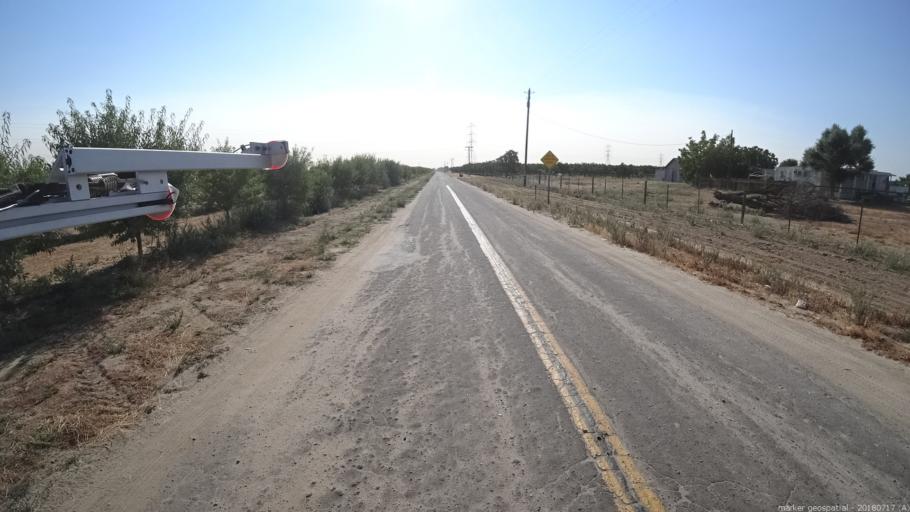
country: US
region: California
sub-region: Madera County
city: Madera Acres
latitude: 37.0400
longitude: -120.1106
